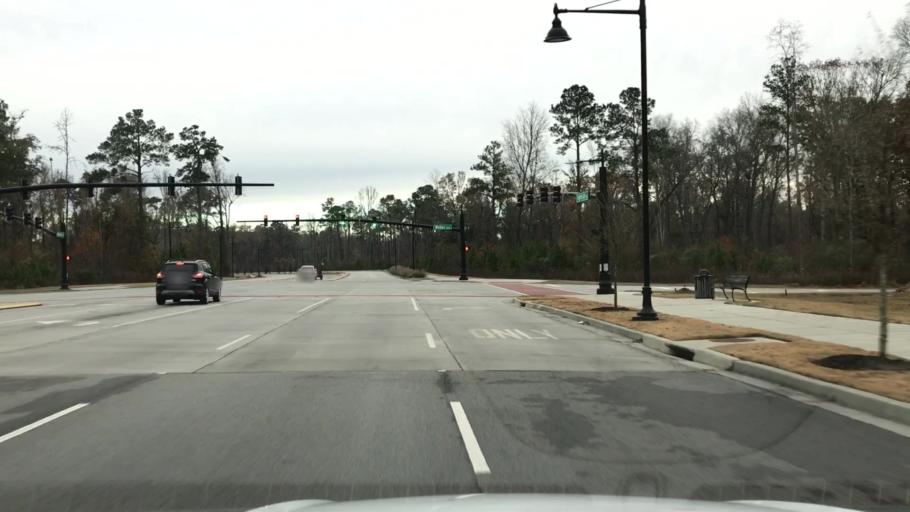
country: US
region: South Carolina
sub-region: Berkeley County
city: Ladson
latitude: 32.9615
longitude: -80.0797
